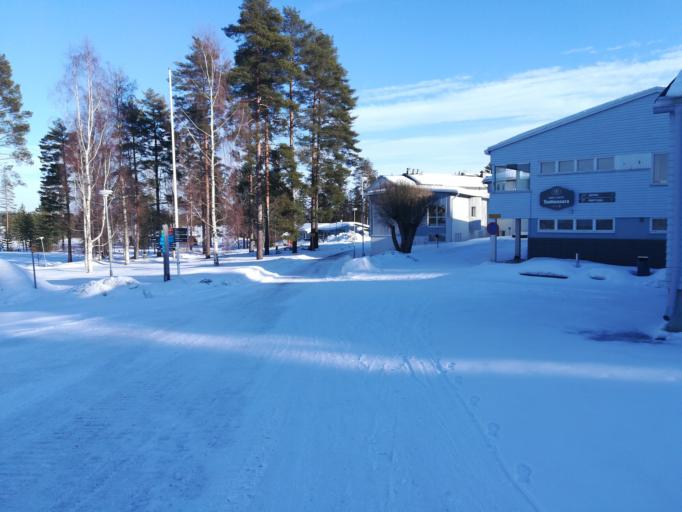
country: FI
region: Southern Savonia
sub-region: Savonlinna
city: Savonlinna
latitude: 61.8075
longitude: 29.0755
